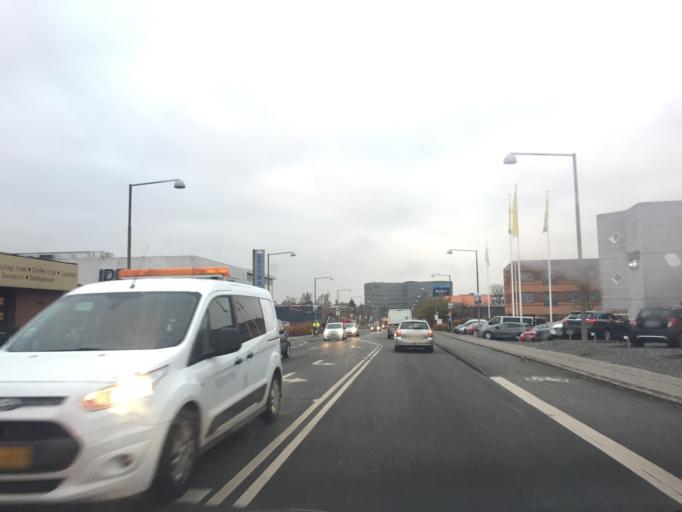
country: DK
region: Capital Region
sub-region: Gladsaxe Municipality
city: Buddinge
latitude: 55.7362
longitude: 12.4867
